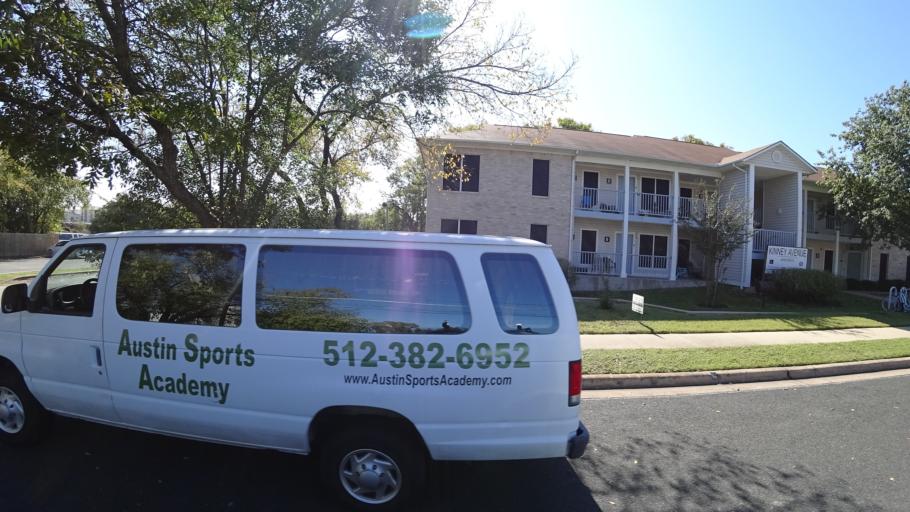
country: US
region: Texas
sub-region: Travis County
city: Austin
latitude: 30.2528
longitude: -97.7673
